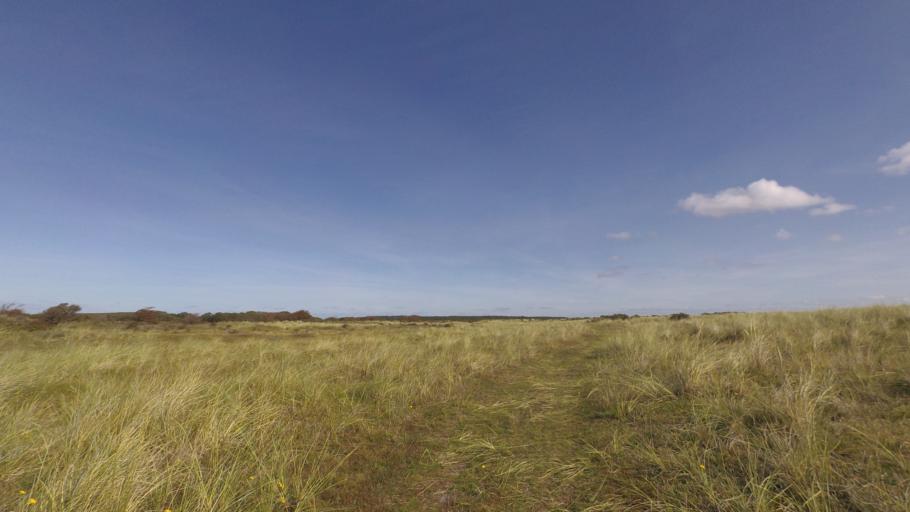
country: NL
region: Friesland
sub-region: Gemeente Ameland
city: Nes
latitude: 53.4498
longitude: 5.7356
